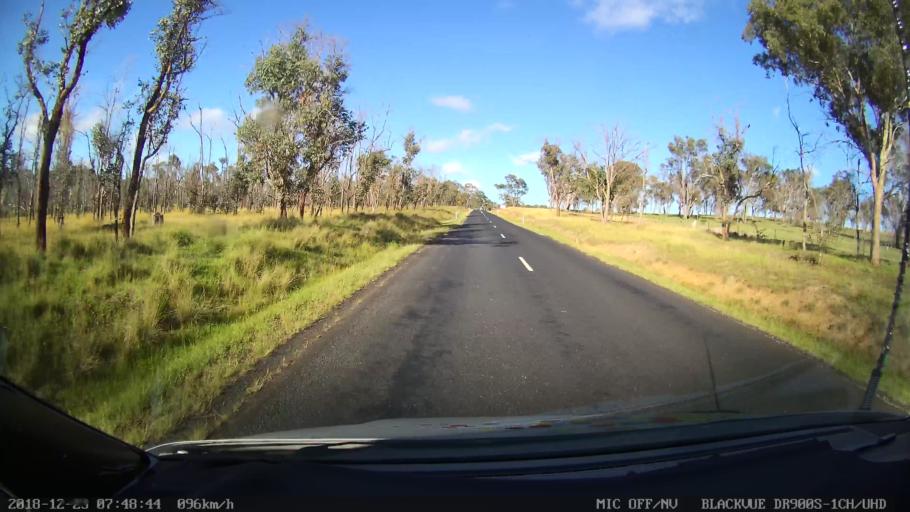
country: AU
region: New South Wales
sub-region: Armidale Dumaresq
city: Armidale
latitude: -30.5336
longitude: 151.8812
